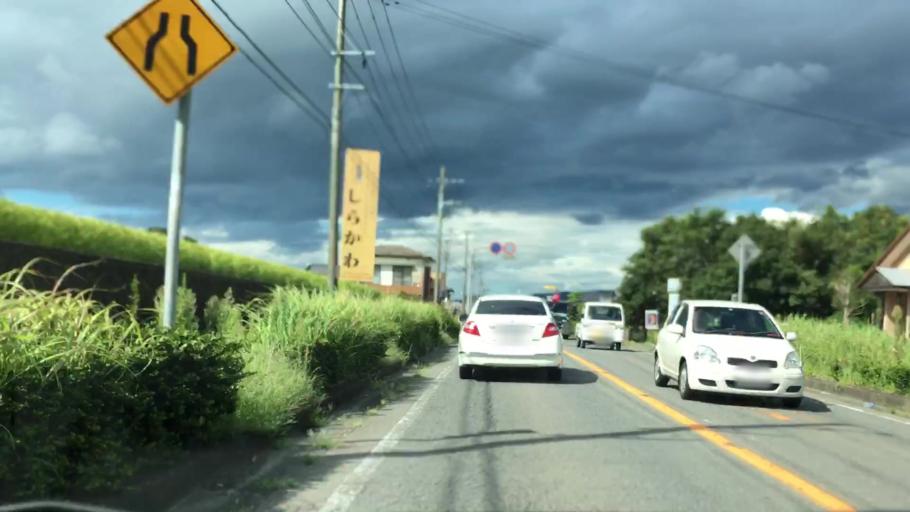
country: JP
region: Saga Prefecture
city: Imaricho-ko
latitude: 33.2428
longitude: 129.8504
